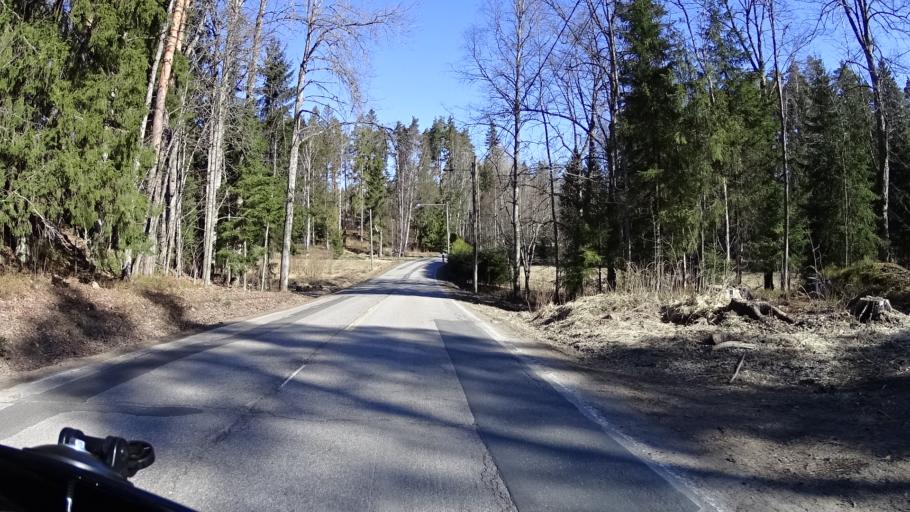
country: FI
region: Uusimaa
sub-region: Helsinki
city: Espoo
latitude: 60.2580
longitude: 24.6525
